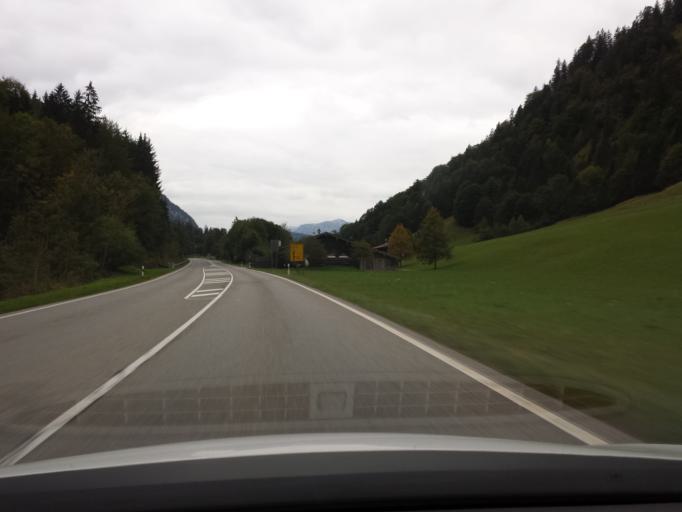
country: DE
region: Bavaria
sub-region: Upper Bavaria
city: Schneizlreuth
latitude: 47.6777
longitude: 12.7678
